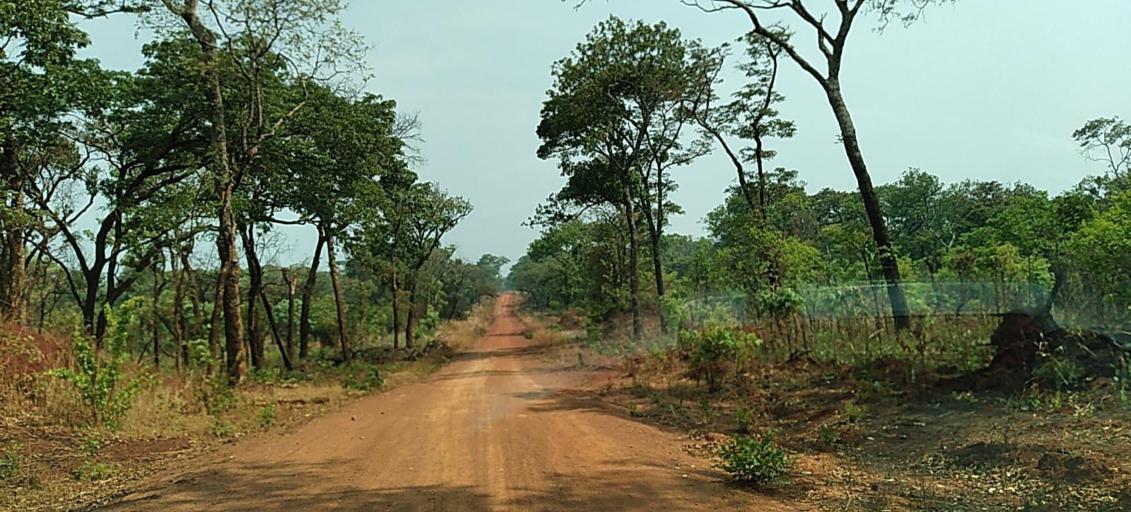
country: ZM
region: North-Western
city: Kansanshi
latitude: -11.9981
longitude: 26.8392
